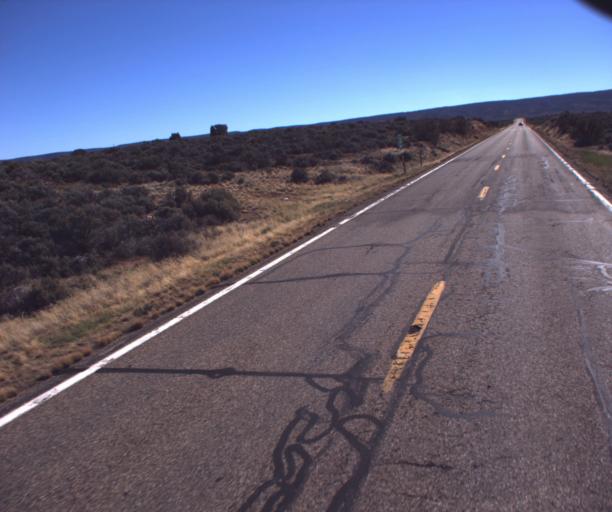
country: US
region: Arizona
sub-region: Coconino County
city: Fredonia
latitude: 36.8660
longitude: -112.3183
